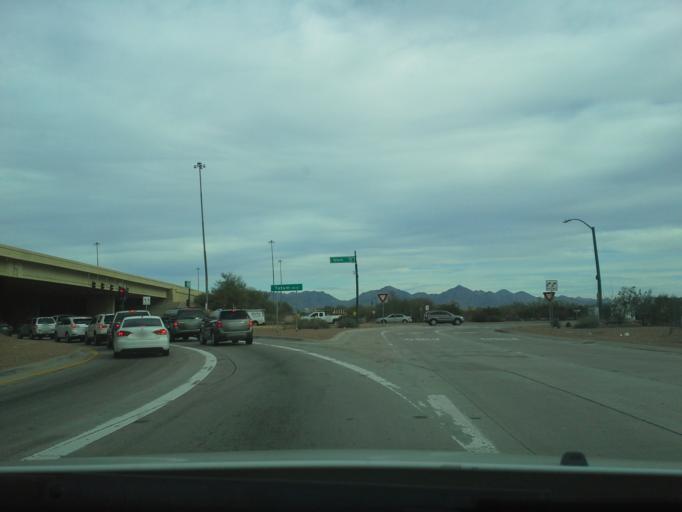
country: US
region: Arizona
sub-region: Maricopa County
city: Paradise Valley
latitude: 33.6725
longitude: -111.9784
